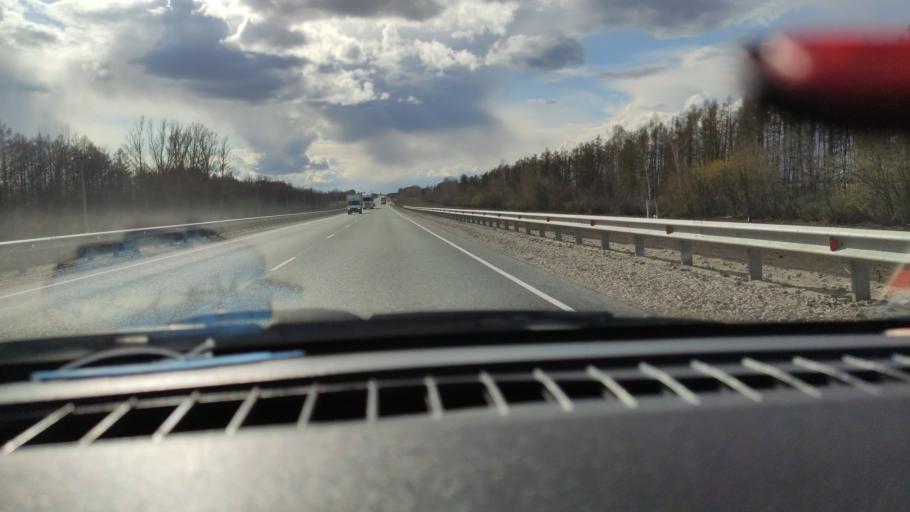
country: RU
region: Saratov
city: Shikhany
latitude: 52.1609
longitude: 47.1286
